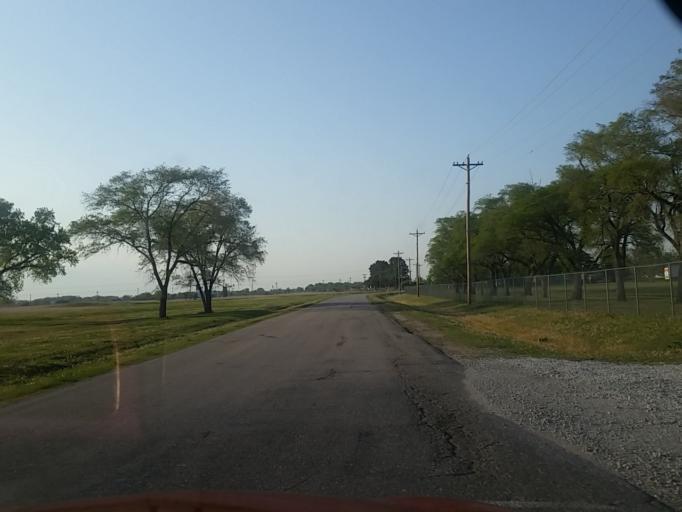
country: US
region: Nebraska
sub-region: Saunders County
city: Ashland
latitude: 41.0598
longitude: -96.3341
